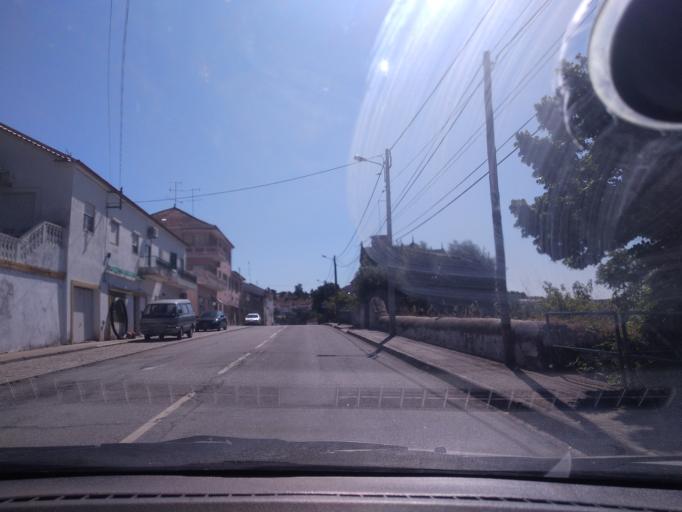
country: PT
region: Portalegre
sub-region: Nisa
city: Nisa
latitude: 39.6528
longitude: -7.6718
